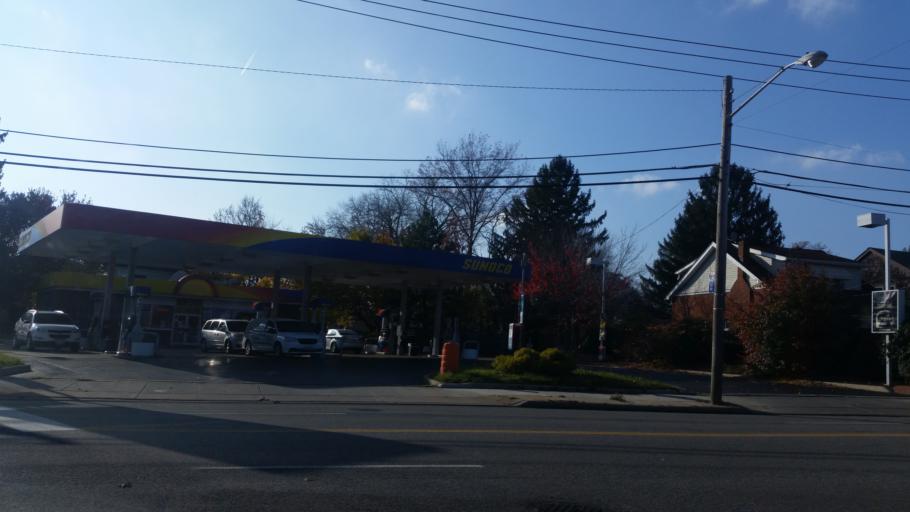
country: US
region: Ohio
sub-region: Cuyahoga County
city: Lakewood
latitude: 41.4557
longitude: -81.8023
